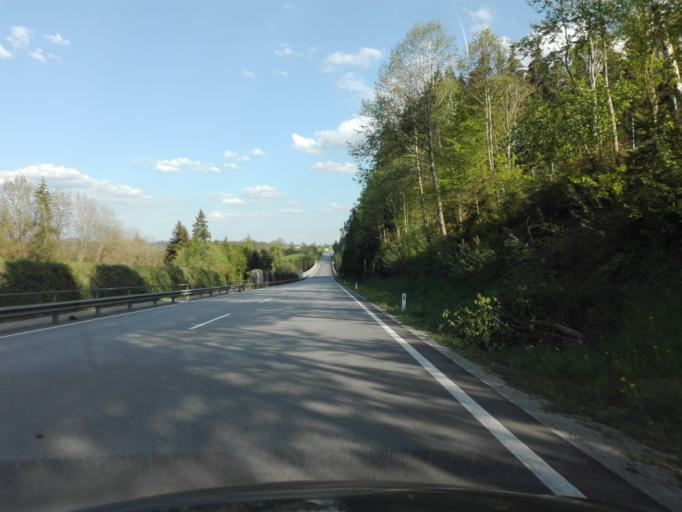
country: AT
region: Upper Austria
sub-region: Politischer Bezirk Rohrbach
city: Kleinzell im Muehlkreis
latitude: 48.4789
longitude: 13.9913
